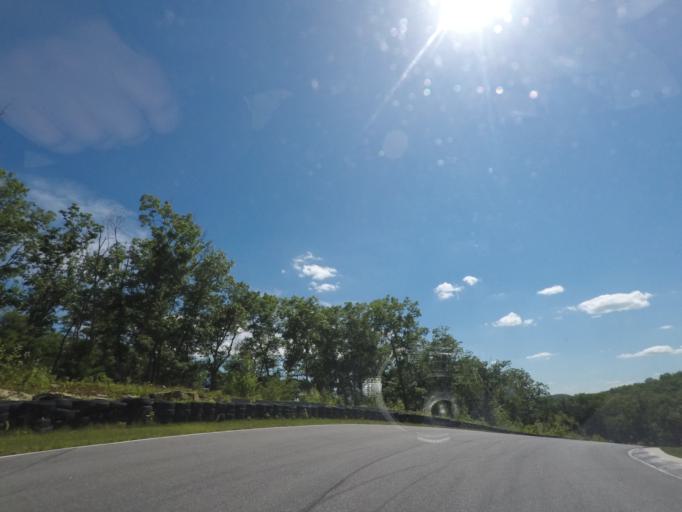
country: US
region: Massachusetts
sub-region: Hampshire County
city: Ware
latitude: 42.2398
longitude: -72.2423
